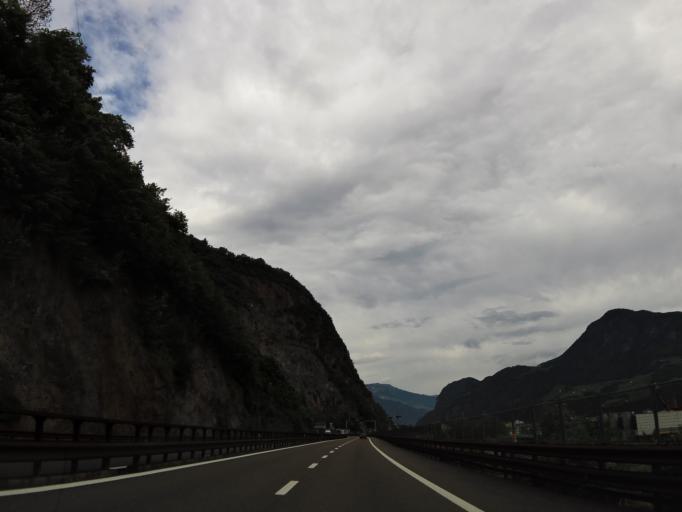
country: IT
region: Trentino-Alto Adige
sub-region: Bolzano
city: Bolzano
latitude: 46.4910
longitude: 11.3639
